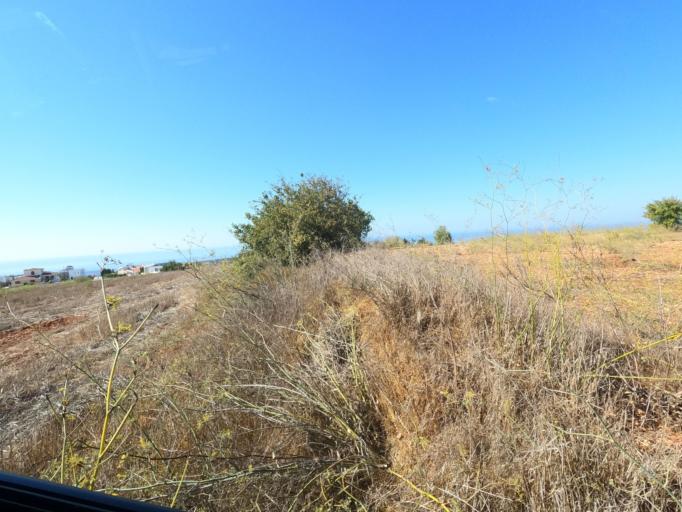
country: CY
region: Pafos
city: Mesogi
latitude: 34.8013
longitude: 32.4888
